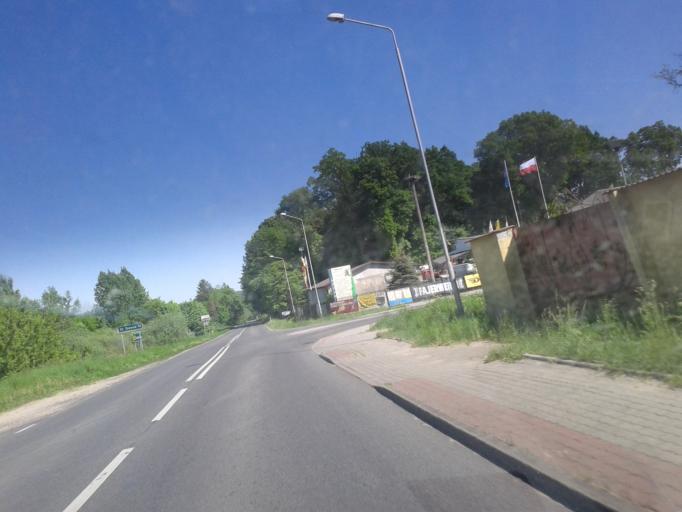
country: PL
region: West Pomeranian Voivodeship
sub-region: Powiat swidwinski
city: Polczyn-Zdroj
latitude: 53.7705
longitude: 16.1361
